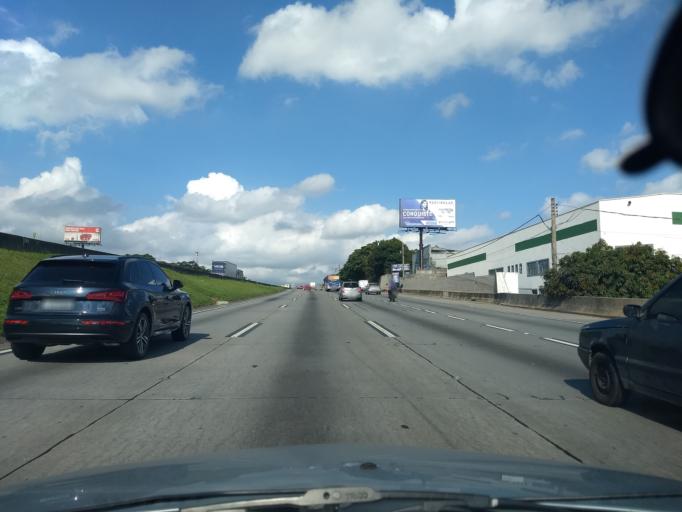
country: BR
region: Sao Paulo
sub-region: Guarulhos
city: Guarulhos
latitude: -23.4577
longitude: -46.4794
